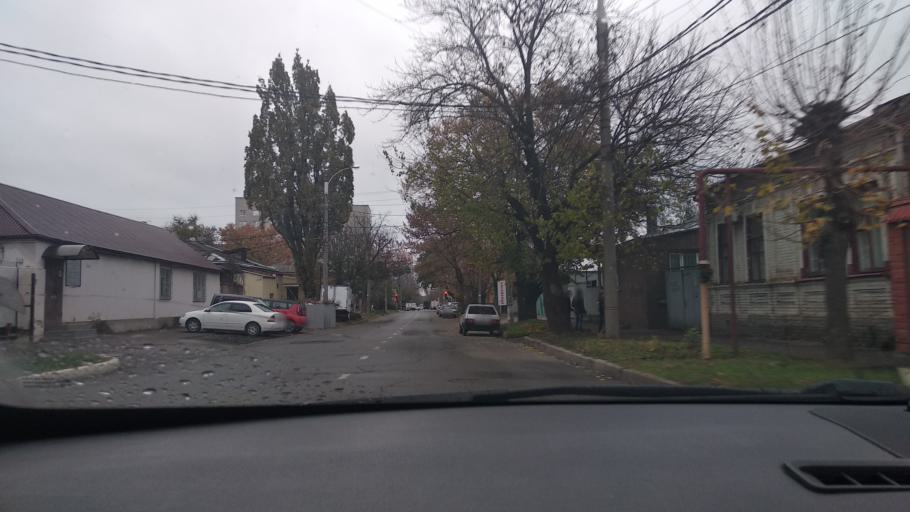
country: RU
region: Krasnodarskiy
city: Krasnodar
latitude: 45.0313
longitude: 38.9840
